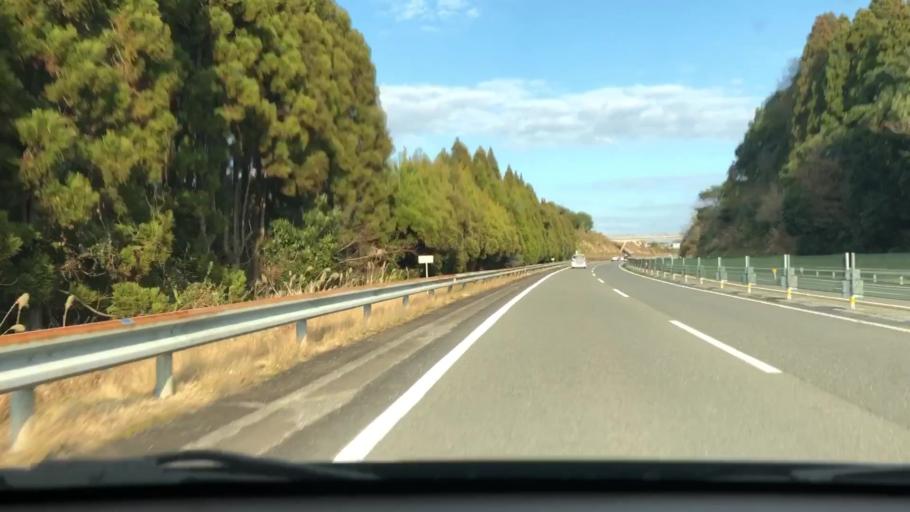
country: JP
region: Miyazaki
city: Miyazaki-shi
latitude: 31.8301
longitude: 131.3148
